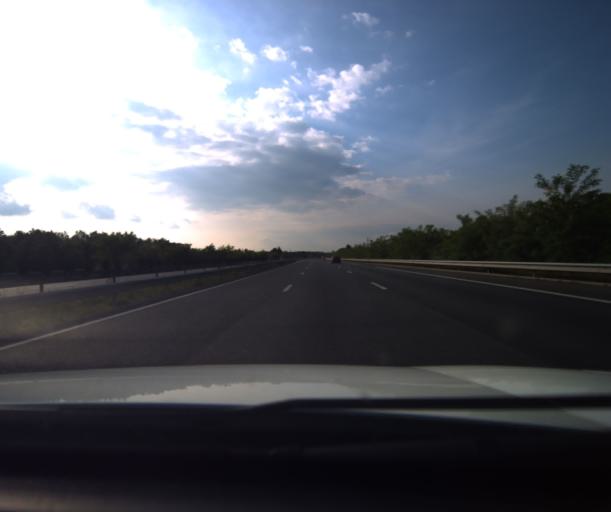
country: FR
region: Midi-Pyrenees
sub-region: Departement de la Haute-Garonne
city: Castelnau-d'Estretefonds
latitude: 43.7946
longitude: 1.3768
